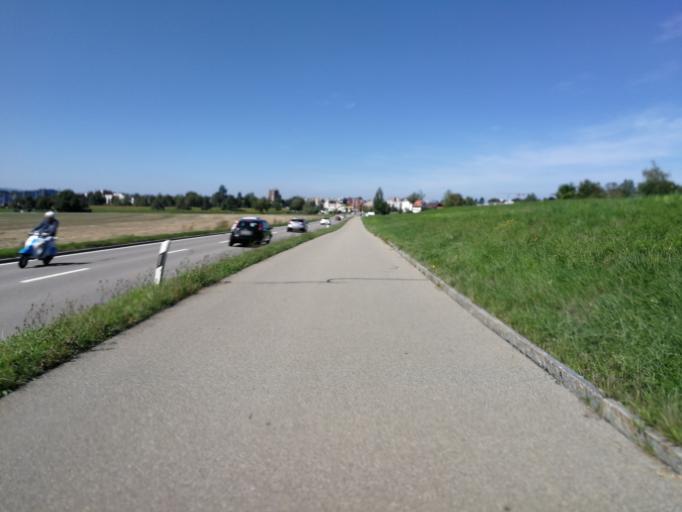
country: CH
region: Zurich
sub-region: Bezirk Hinwil
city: Wetzikon / Kempten
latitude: 47.3251
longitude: 8.8191
